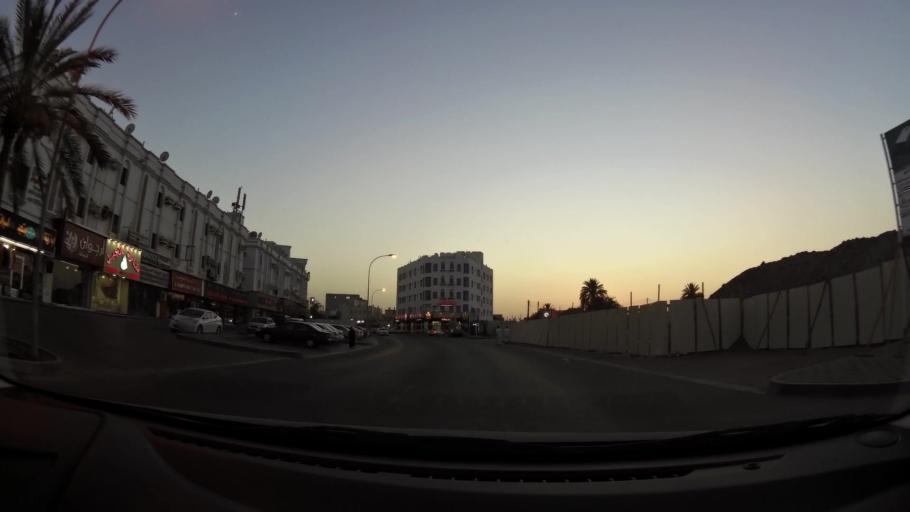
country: OM
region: Muhafazat Masqat
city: As Sib al Jadidah
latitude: 23.6842
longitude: 58.1761
